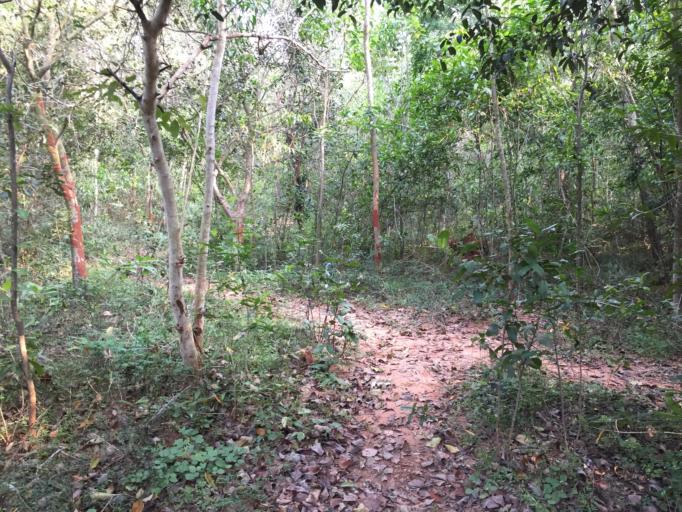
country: IN
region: Tamil Nadu
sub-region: Villupuram
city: Auroville
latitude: 12.0123
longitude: 79.8144
